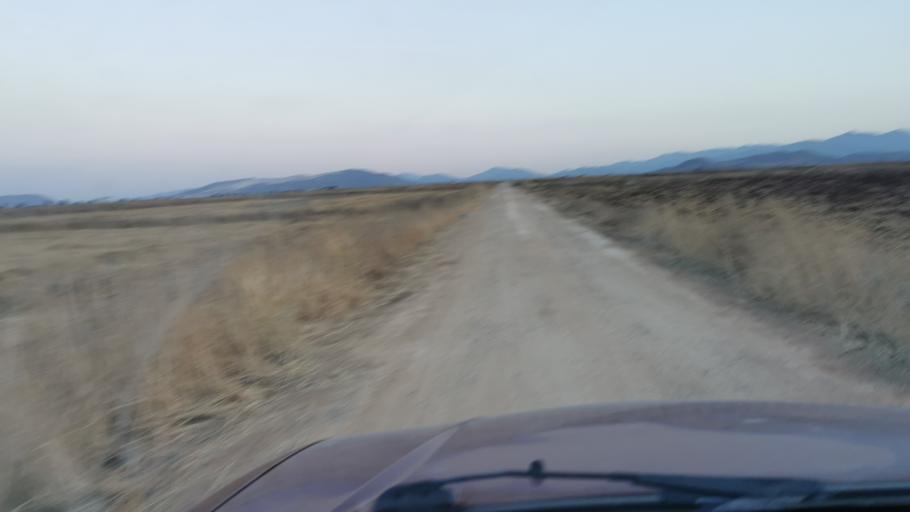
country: CY
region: Lefkosia
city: Peristerona
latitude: 35.0984
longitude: 33.0779
